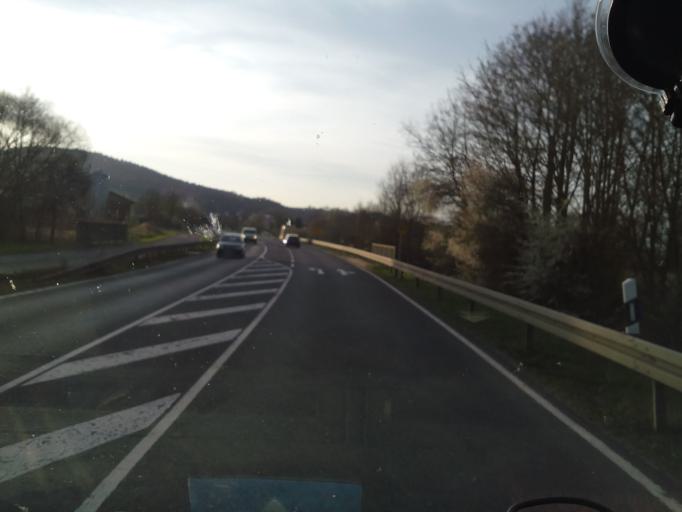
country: DE
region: Bavaria
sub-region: Upper Franconia
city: Reckendorf
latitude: 50.0034
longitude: 10.8371
